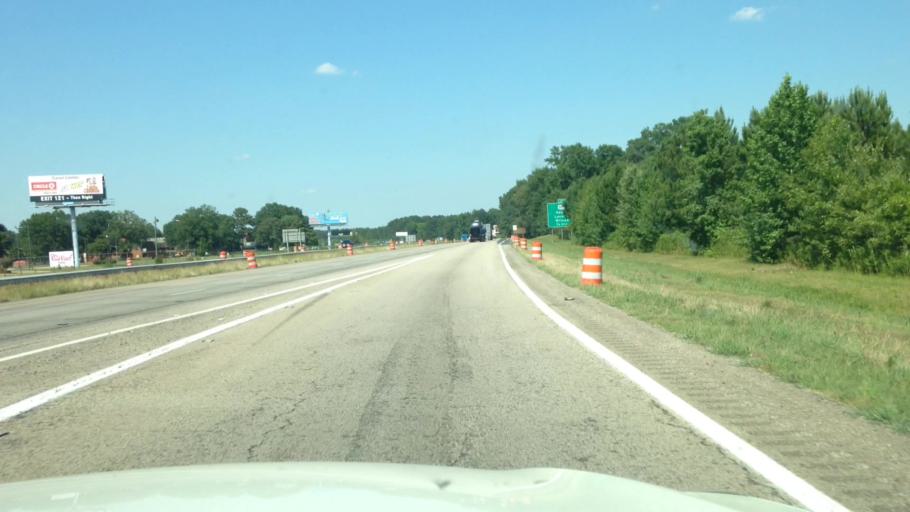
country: US
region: North Carolina
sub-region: Johnston County
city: Kenly
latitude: 35.5805
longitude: -78.1432
